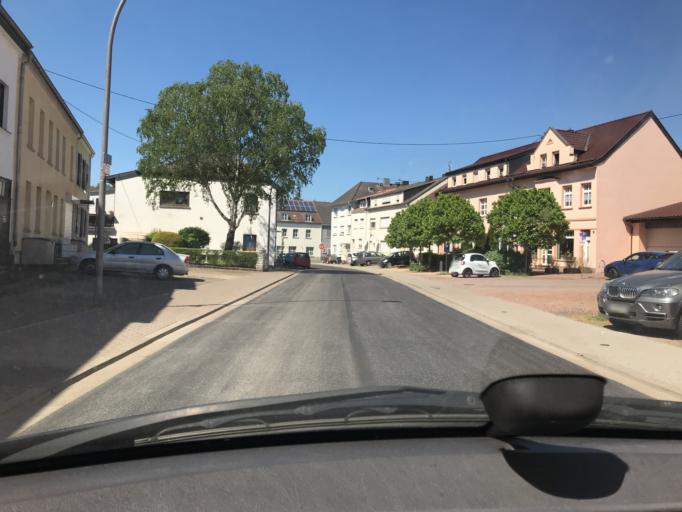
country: DE
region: Saarland
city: Saarlouis
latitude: 49.3299
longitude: 6.7455
